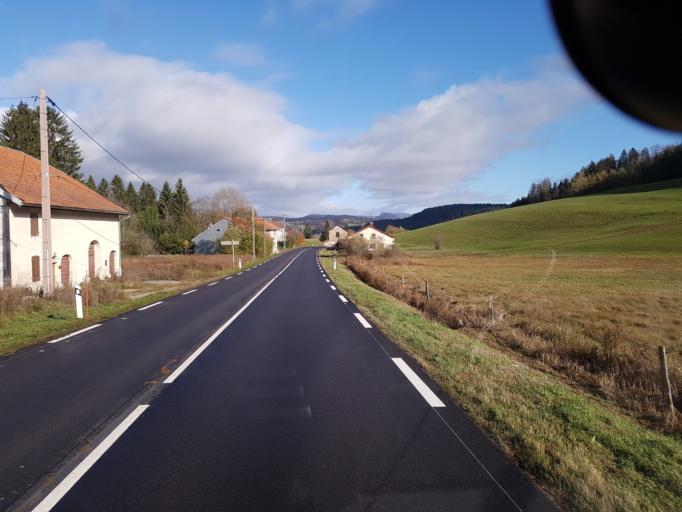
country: FR
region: Franche-Comte
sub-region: Departement du Jura
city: Morbier
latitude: 46.5942
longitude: 5.9570
